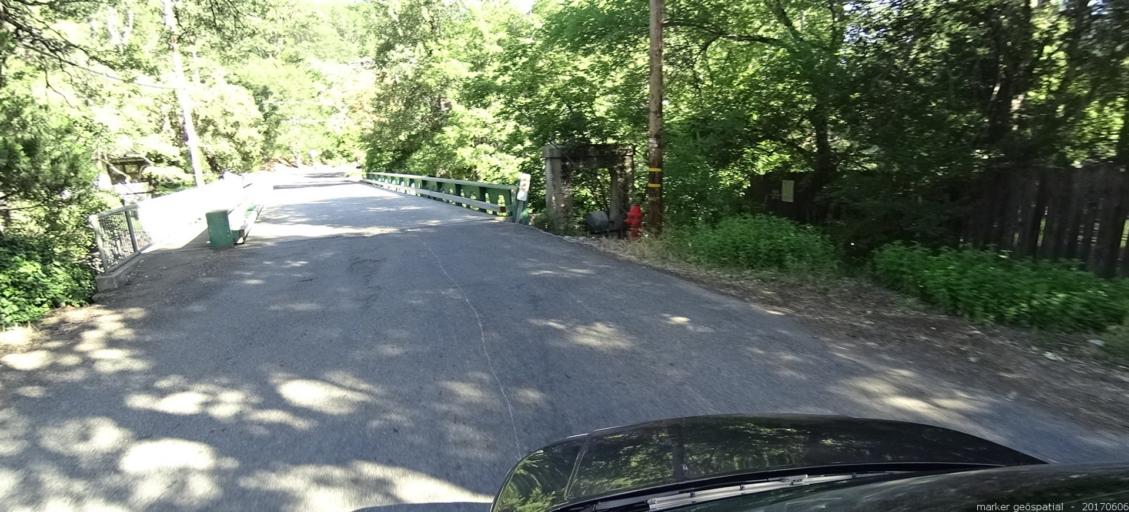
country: US
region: California
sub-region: Siskiyou County
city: Dunsmuir
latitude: 41.2021
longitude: -122.2725
